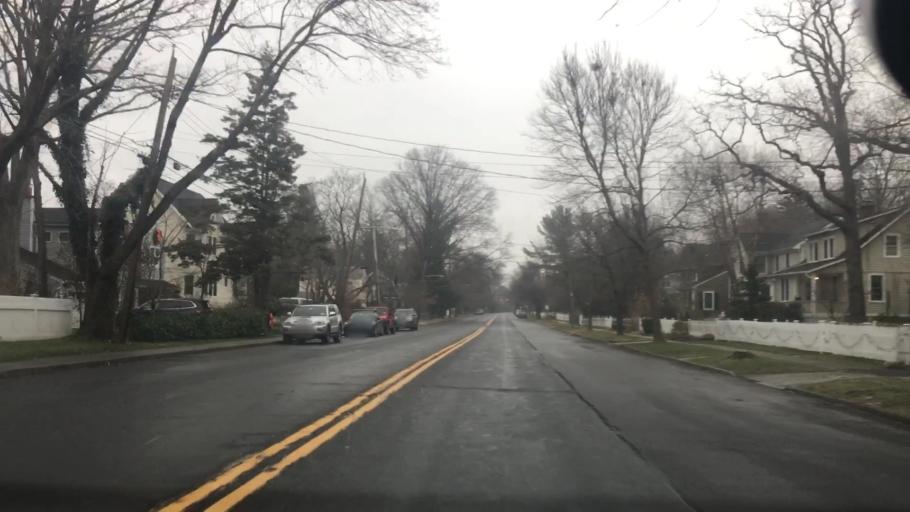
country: US
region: New York
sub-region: Westchester County
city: Rye
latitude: 40.9682
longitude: -73.6839
